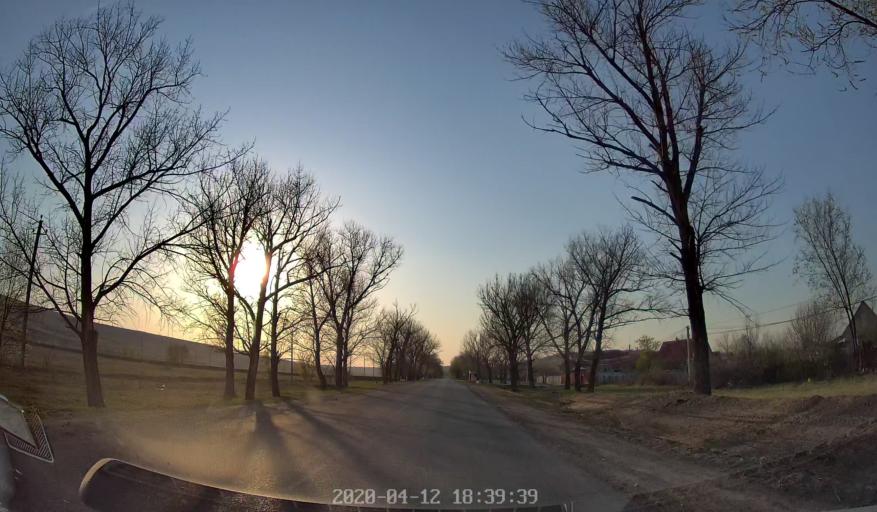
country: MD
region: Chisinau
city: Ciorescu
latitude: 47.1291
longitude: 28.9813
